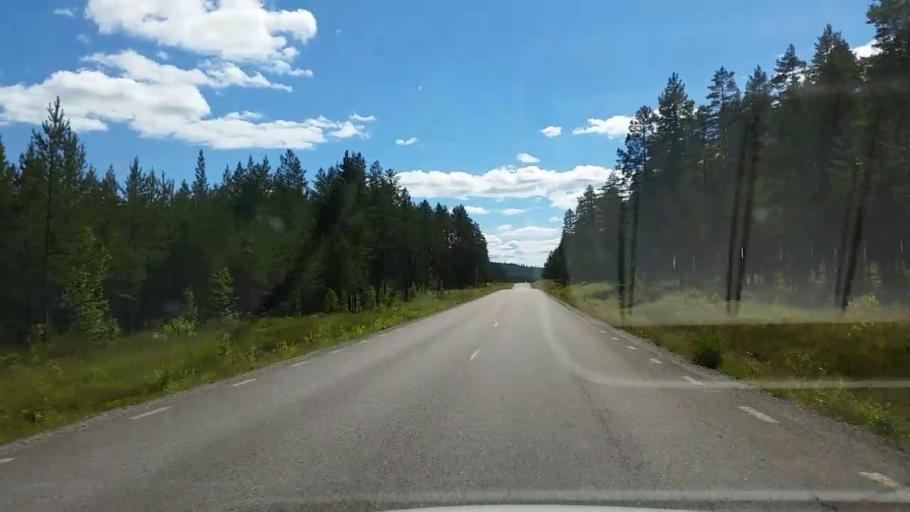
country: SE
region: Dalarna
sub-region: Faluns Kommun
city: Svardsjo
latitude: 61.0210
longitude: 15.7580
